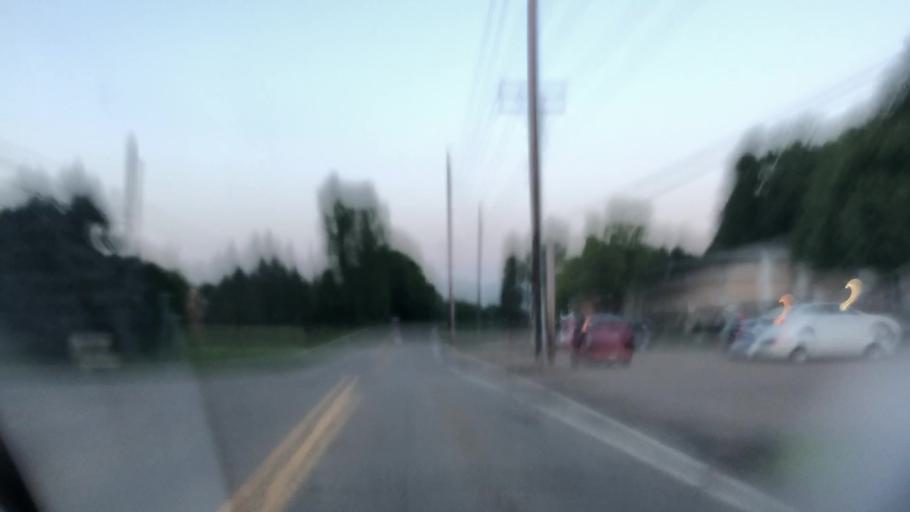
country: US
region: Ohio
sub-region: Stark County
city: Perry Heights
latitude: 40.8320
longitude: -81.4945
